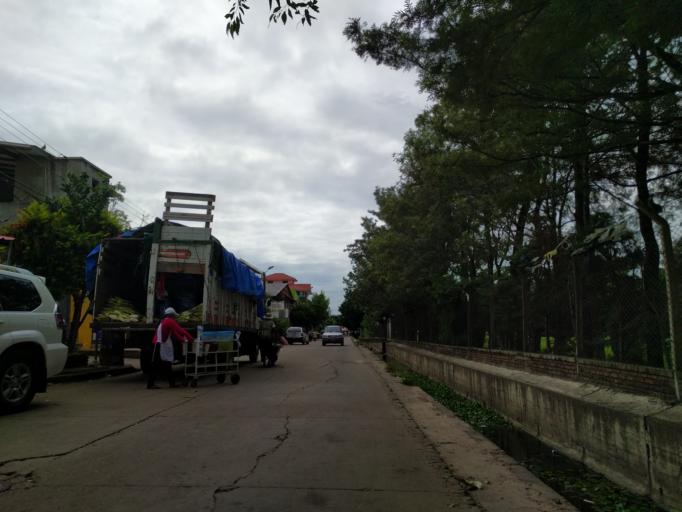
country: BO
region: Santa Cruz
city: Santa Cruz de la Sierra
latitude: -17.7986
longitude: -63.2067
